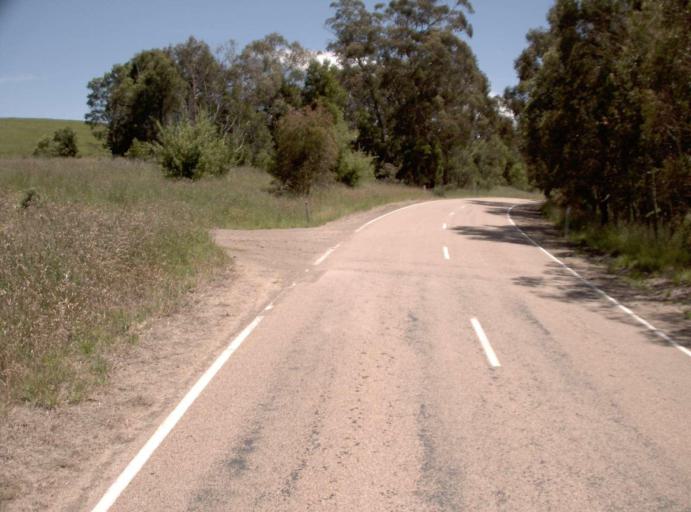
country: AU
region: Victoria
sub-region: East Gippsland
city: Lakes Entrance
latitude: -37.2137
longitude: 148.2682
